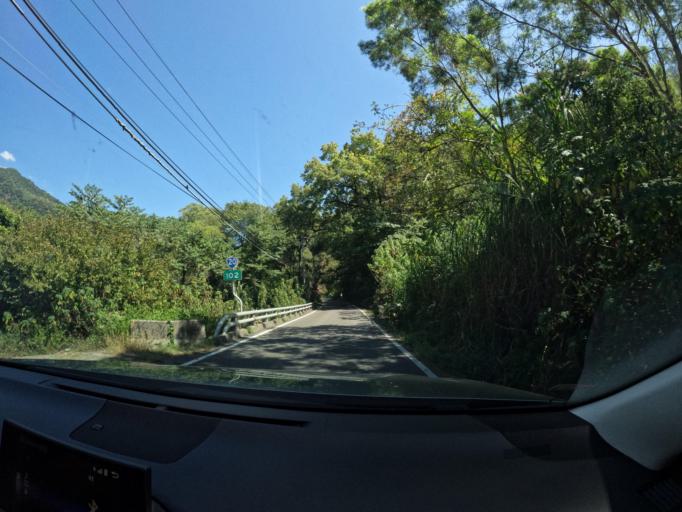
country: TW
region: Taiwan
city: Yujing
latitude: 23.2430
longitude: 120.8137
